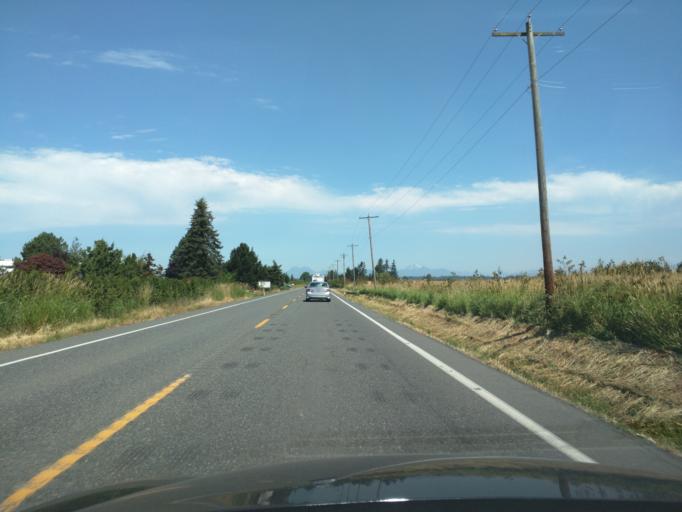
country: US
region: Washington
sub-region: Whatcom County
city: Lynden
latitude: 48.9536
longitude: -122.4852
